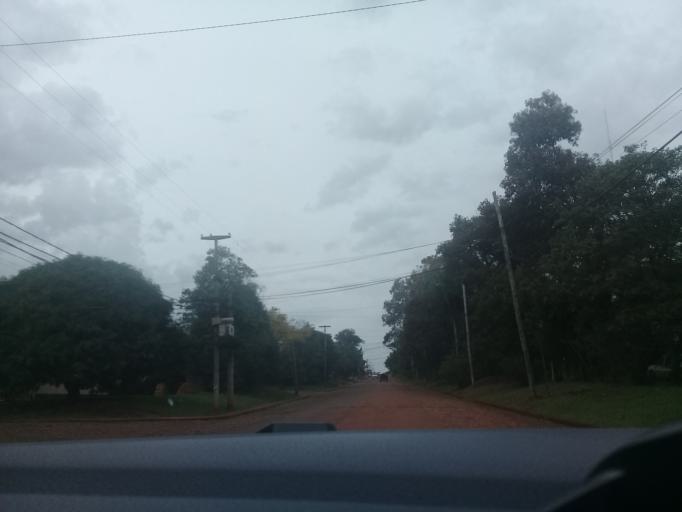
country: AR
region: Misiones
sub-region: Departamento de Obera
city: Obera
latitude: -27.4818
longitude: -55.1525
